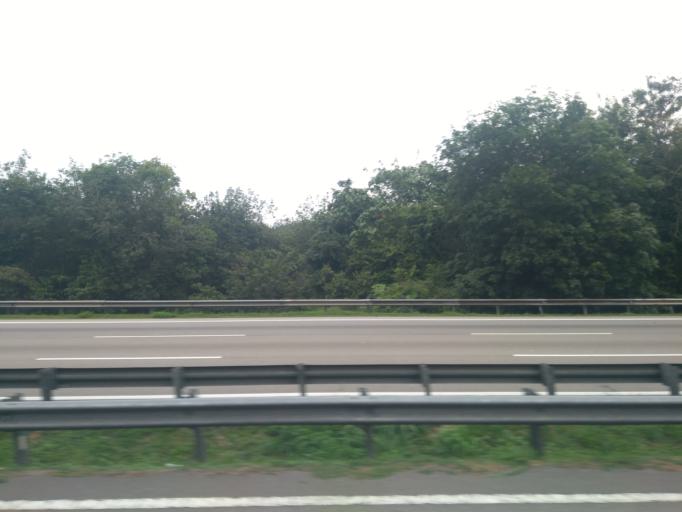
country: MY
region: Melaka
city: Pulau Sebang
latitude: 2.4466
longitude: 102.1745
